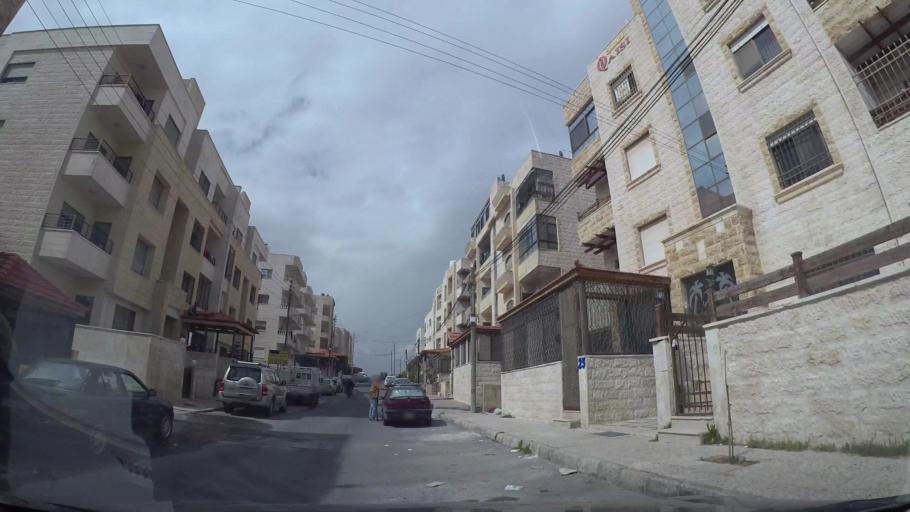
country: JO
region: Amman
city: Amman
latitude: 31.9889
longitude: 35.9217
